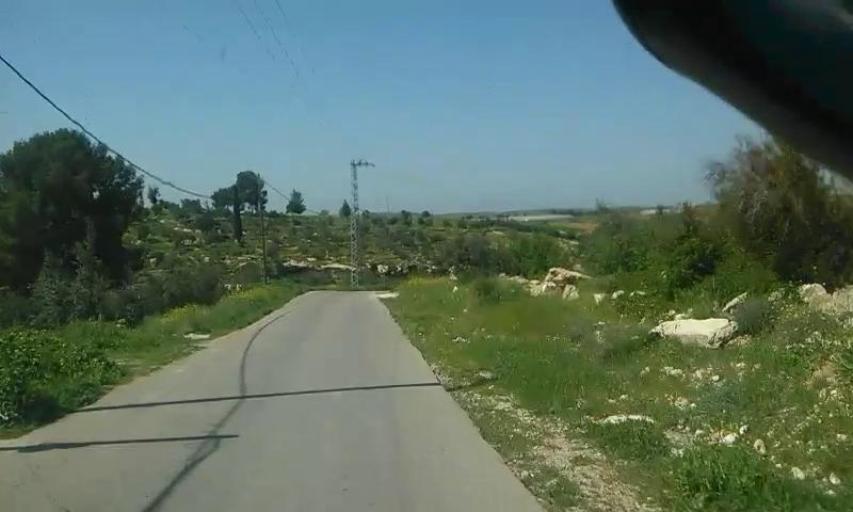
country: PS
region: West Bank
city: Al Majd
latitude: 31.4872
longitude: 34.9437
